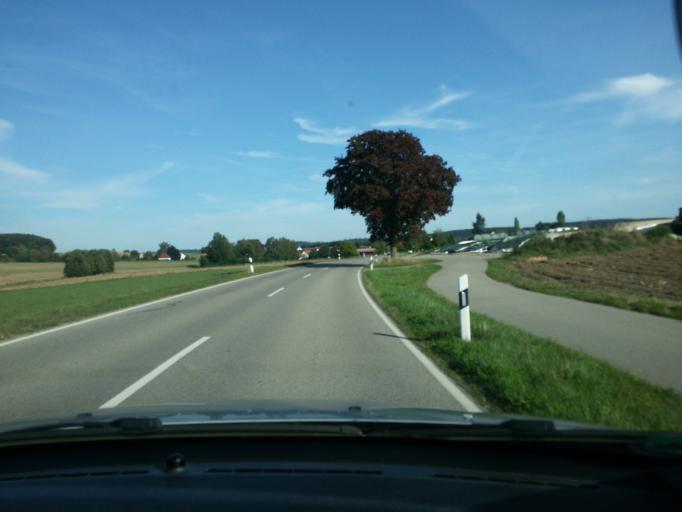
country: DE
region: Bavaria
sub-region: Swabia
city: Gessertshausen
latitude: 48.3479
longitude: 10.7245
